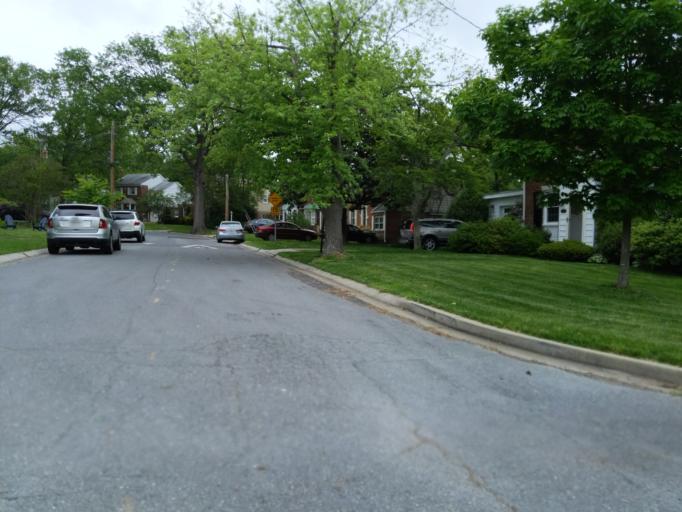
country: US
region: Maryland
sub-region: Montgomery County
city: Wheaton
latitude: 39.0292
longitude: -77.0443
